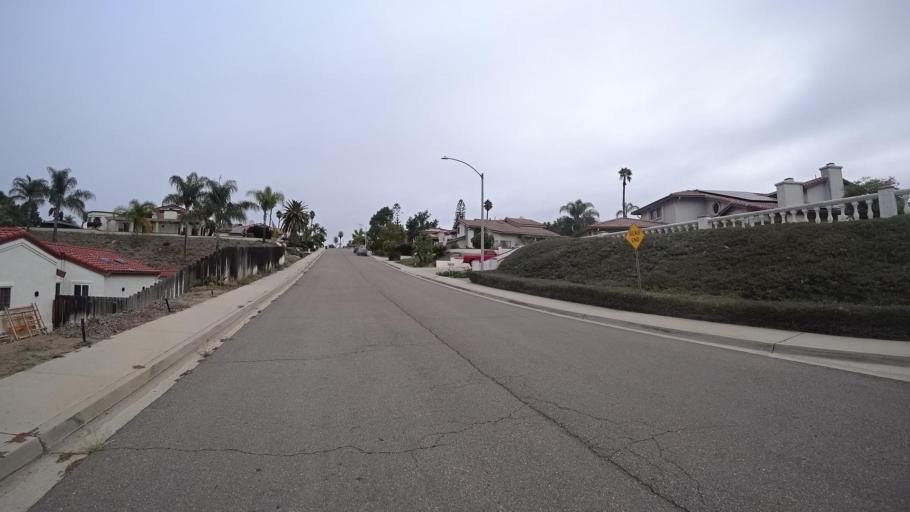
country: US
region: California
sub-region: San Diego County
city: Rancho San Diego
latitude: 32.7581
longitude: -116.9144
